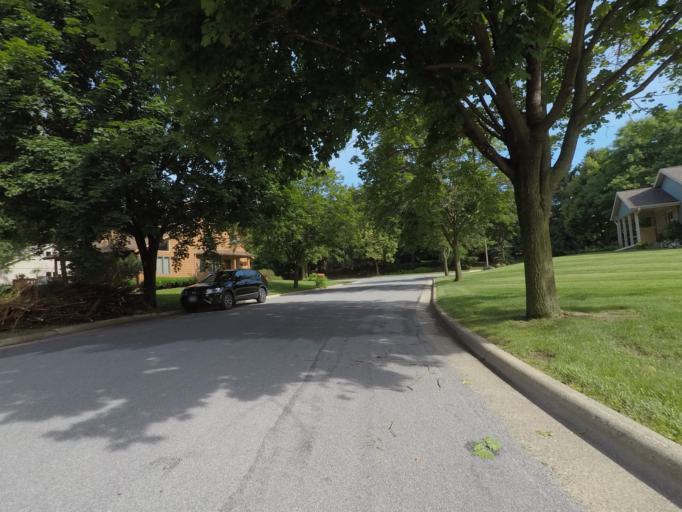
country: US
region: Wisconsin
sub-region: Dane County
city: Middleton
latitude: 43.0770
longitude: -89.4971
